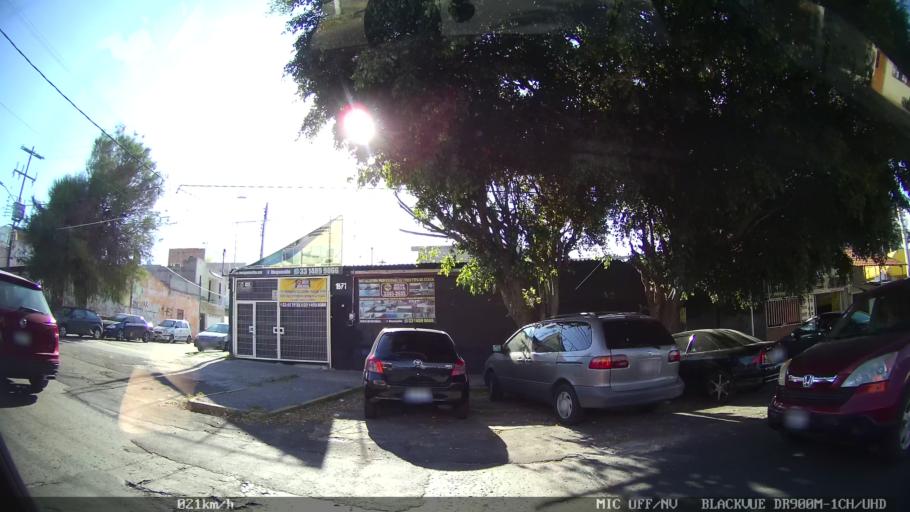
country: MX
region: Jalisco
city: Tlaquepaque
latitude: 20.6980
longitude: -103.3210
